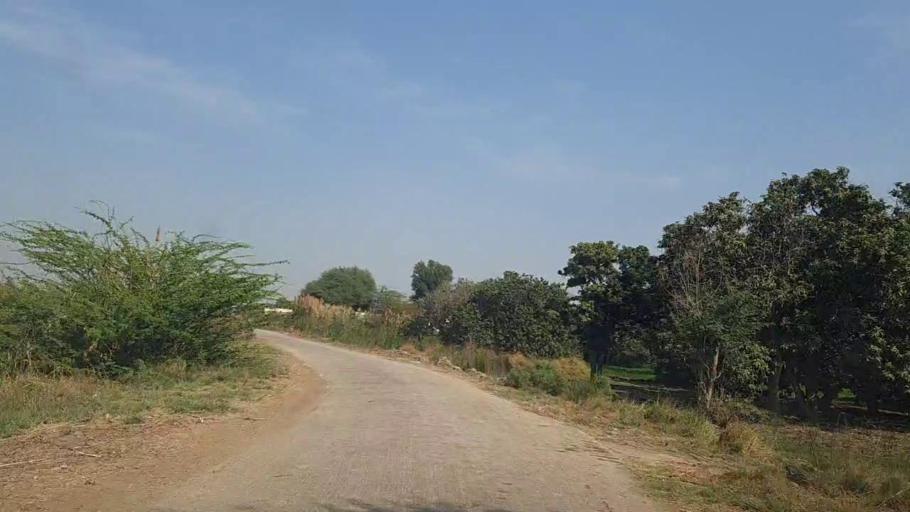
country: PK
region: Sindh
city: Mirpur Khas
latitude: 25.4931
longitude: 68.9213
